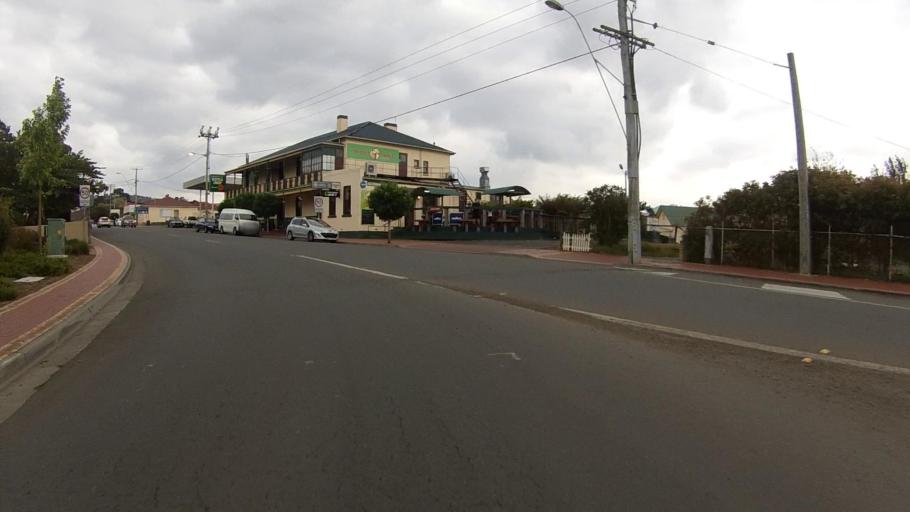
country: AU
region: Tasmania
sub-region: Huon Valley
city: Cygnet
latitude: -43.1633
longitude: 147.0796
